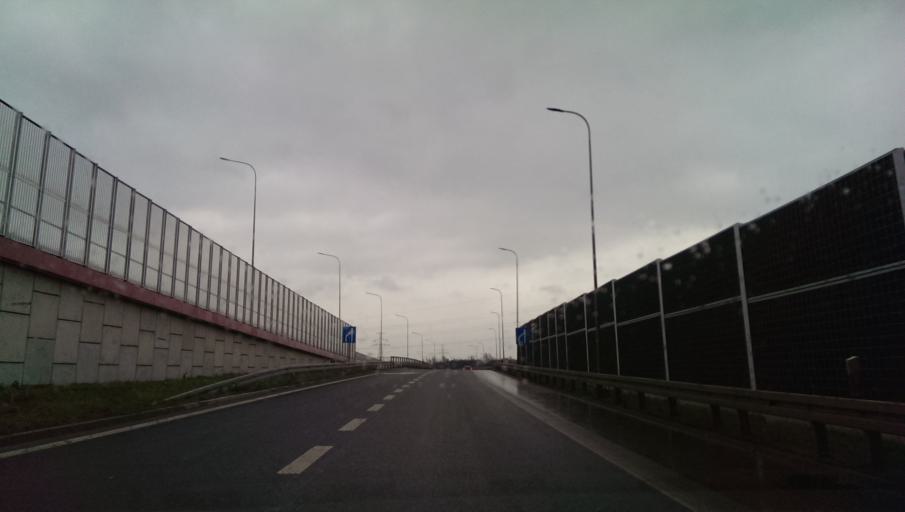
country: PL
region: Lesser Poland Voivodeship
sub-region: Powiat wielicki
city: Kokotow
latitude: 50.0633
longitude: 20.0733
